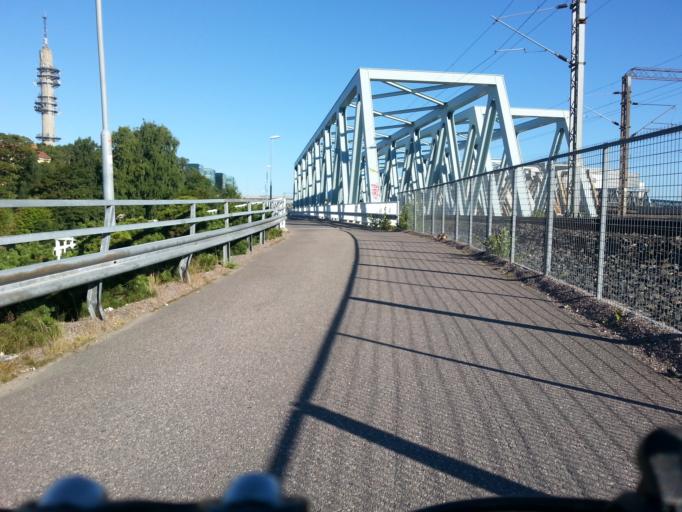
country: FI
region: Uusimaa
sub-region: Helsinki
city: Helsinki
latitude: 60.2026
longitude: 24.9306
